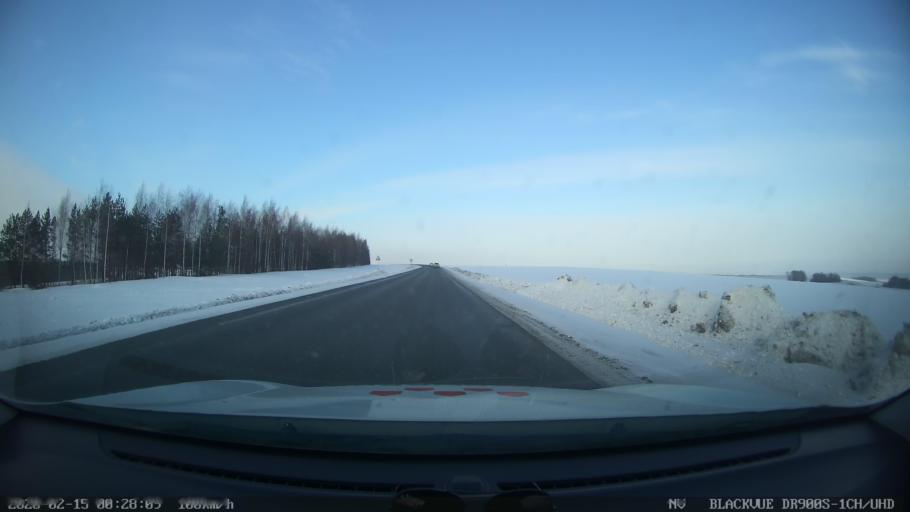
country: RU
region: Tatarstan
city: Verkhniy Uslon
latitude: 55.6382
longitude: 48.8741
